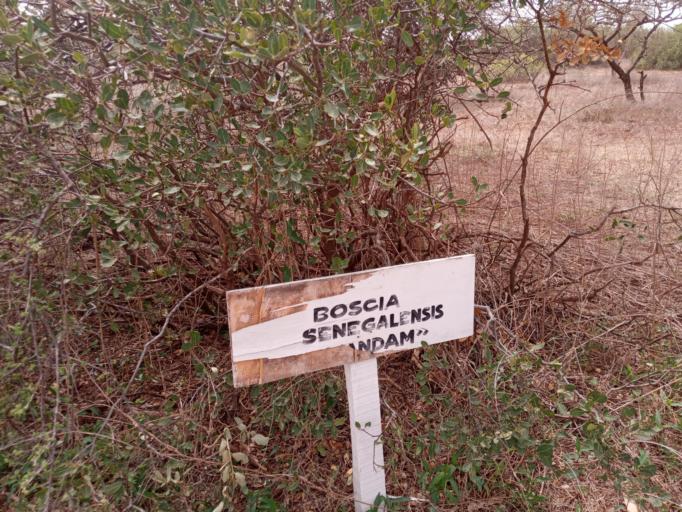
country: SN
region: Saint-Louis
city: Saint-Louis
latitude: 15.9213
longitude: -16.4528
